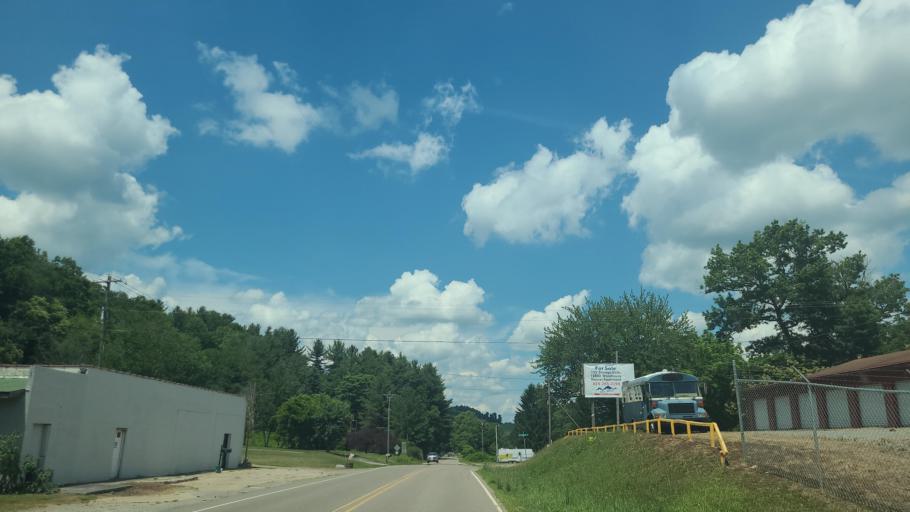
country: US
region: North Carolina
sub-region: Watauga County
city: Boone
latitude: 36.2350
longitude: -81.5464
